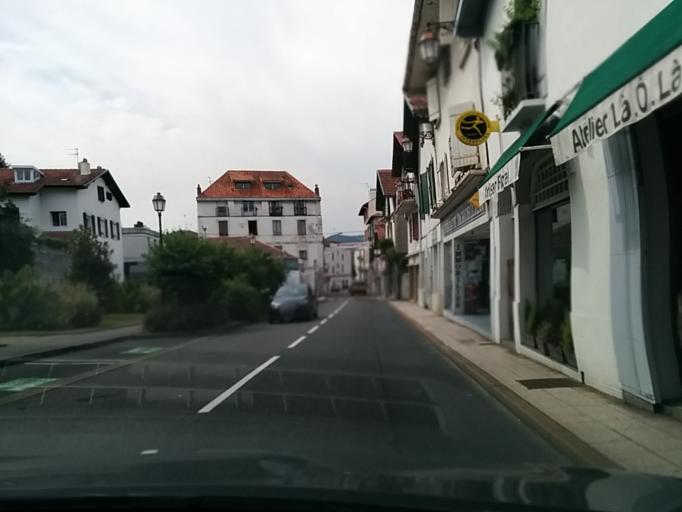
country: FR
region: Aquitaine
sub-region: Departement des Pyrenees-Atlantiques
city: Hendaye
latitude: 43.3593
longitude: -1.7758
